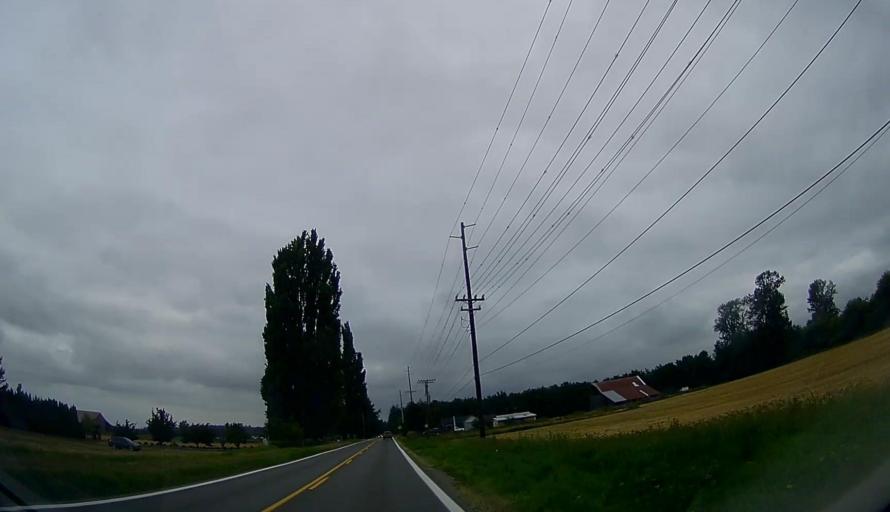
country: US
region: Washington
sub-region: Snohomish County
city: Stanwood
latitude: 48.2154
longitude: -122.3351
